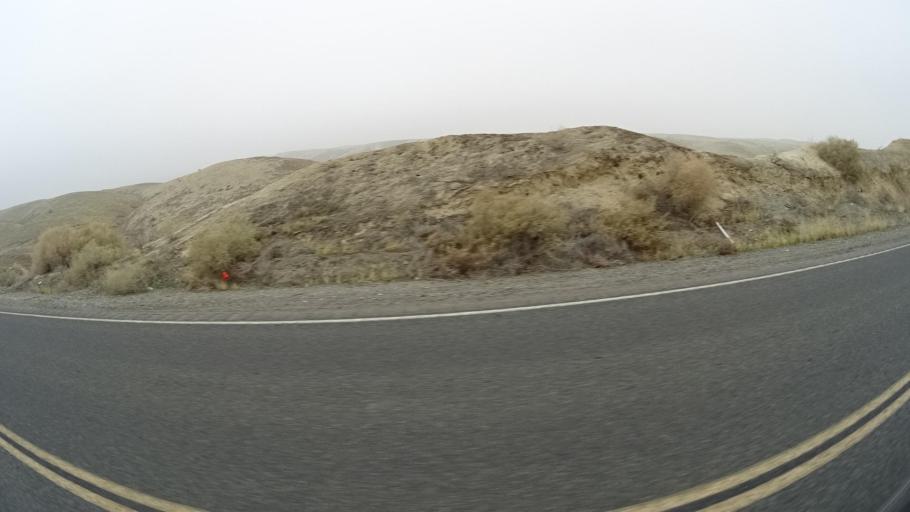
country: US
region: California
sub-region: Kern County
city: Buttonwillow
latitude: 35.3230
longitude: -119.4654
